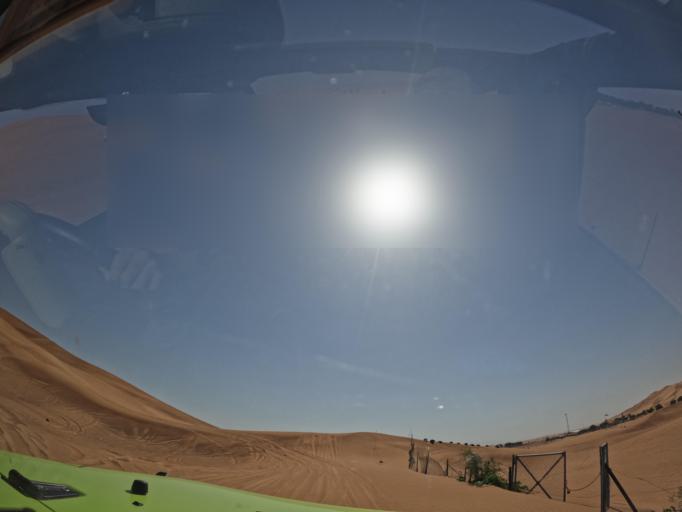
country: AE
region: Ash Shariqah
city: Adh Dhayd
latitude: 24.9582
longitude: 55.7162
